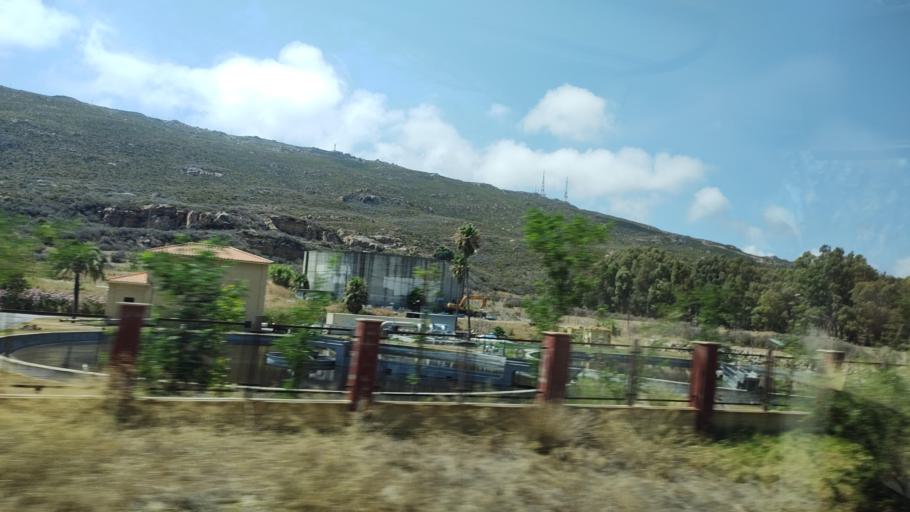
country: ES
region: Andalusia
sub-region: Provincia de Cadiz
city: La Linea de la Concepcion
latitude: 36.1948
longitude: -5.3477
